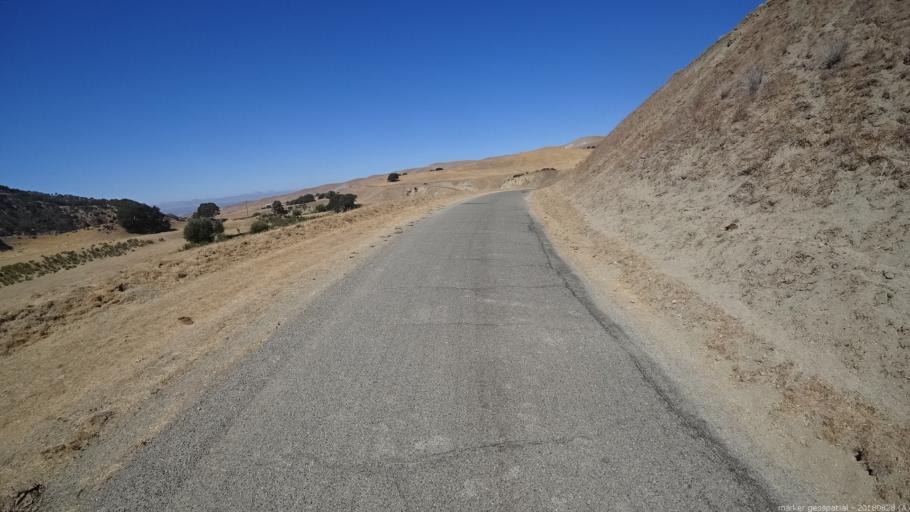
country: US
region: California
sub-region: San Luis Obispo County
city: San Miguel
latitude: 36.0677
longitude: -120.7728
